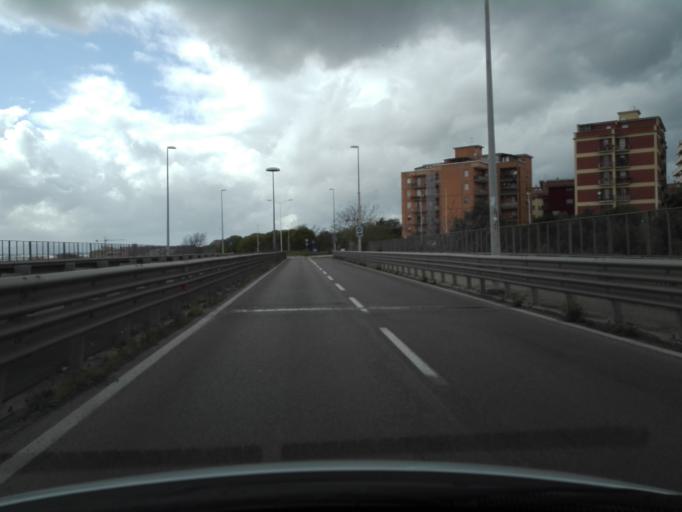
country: IT
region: Sardinia
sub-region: Provincia di Sassari
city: Sassari
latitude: 40.7319
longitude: 8.5708
